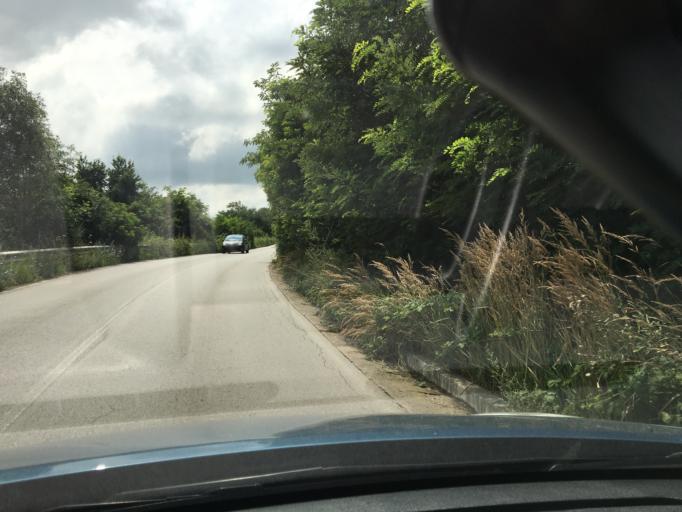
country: BG
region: Sofia-Capital
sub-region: Stolichna Obshtina
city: Sofia
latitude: 42.6028
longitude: 23.3683
